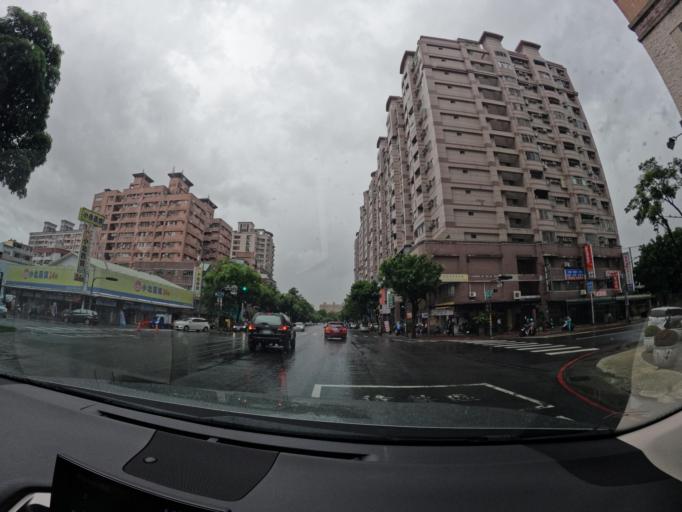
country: TW
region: Kaohsiung
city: Kaohsiung
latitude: 22.6599
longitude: 120.3289
